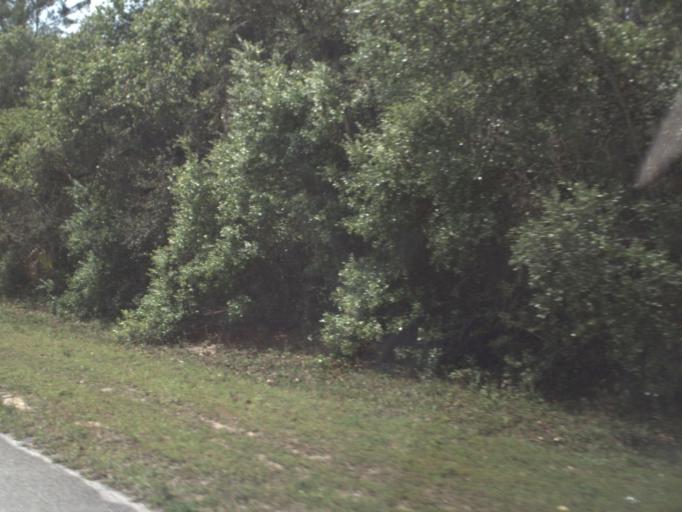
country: US
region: Florida
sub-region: Lake County
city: Astor
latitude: 29.2800
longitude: -81.6491
